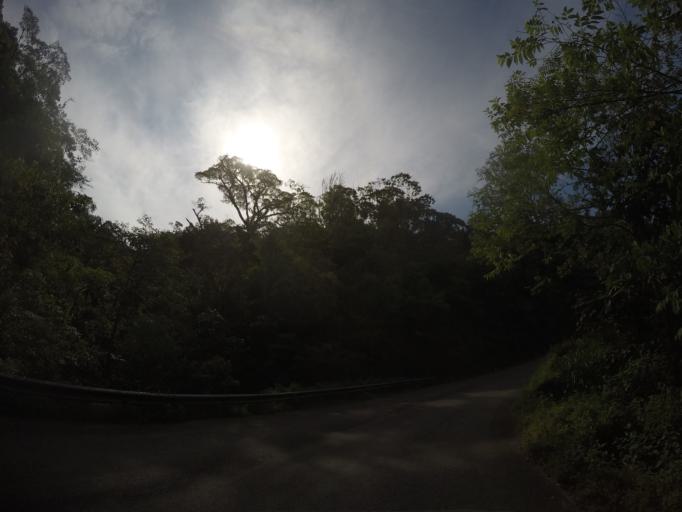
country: MX
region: Oaxaca
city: Pluma Hidalgo
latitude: 15.9339
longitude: -96.4259
